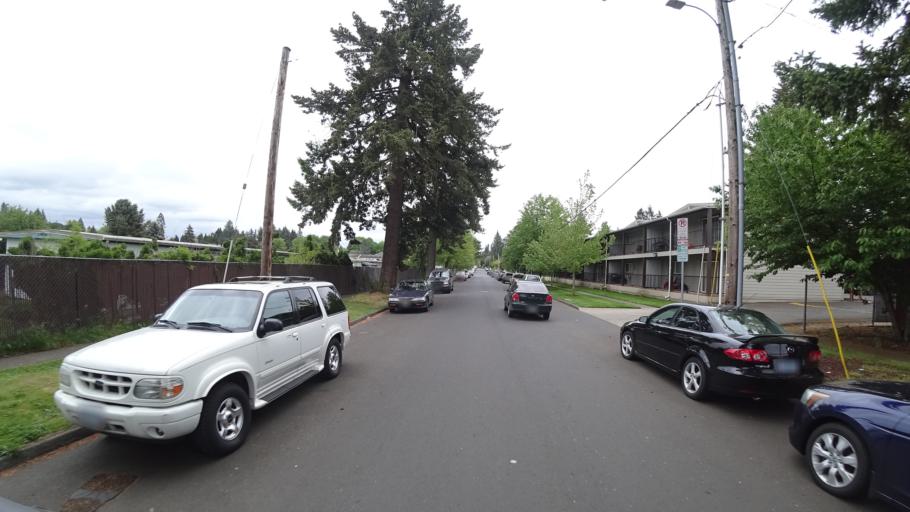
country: US
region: Oregon
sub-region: Washington County
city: Beaverton
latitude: 45.4757
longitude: -122.8043
